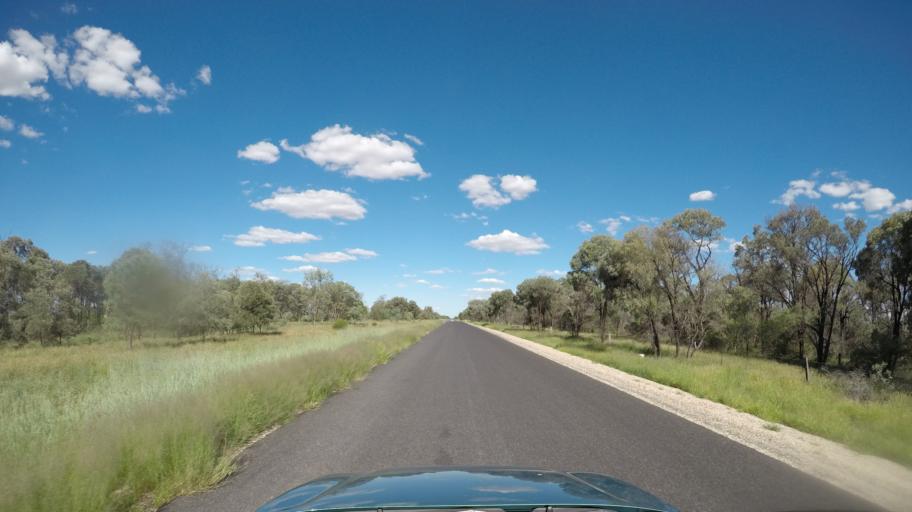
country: AU
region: Queensland
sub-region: Goondiwindi
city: Goondiwindi
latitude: -28.1671
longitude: 150.1871
